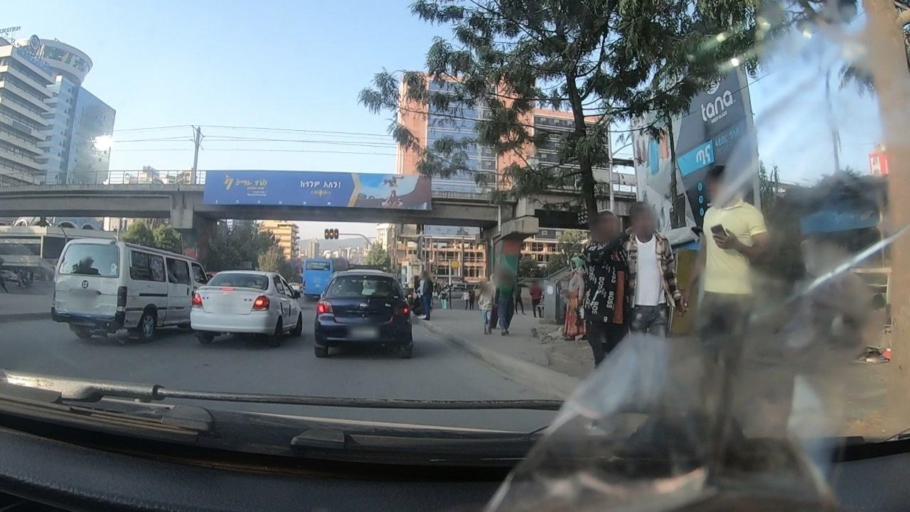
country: ET
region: Adis Abeba
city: Addis Ababa
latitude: 9.0114
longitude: 38.7533
